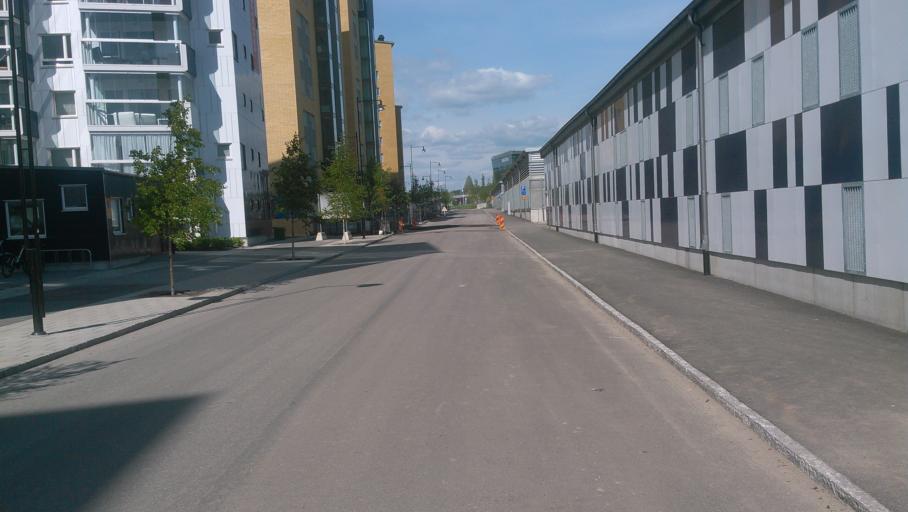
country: SE
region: Vaesterbotten
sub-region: Umea Kommun
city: Umea
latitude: 63.8149
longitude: 20.2935
